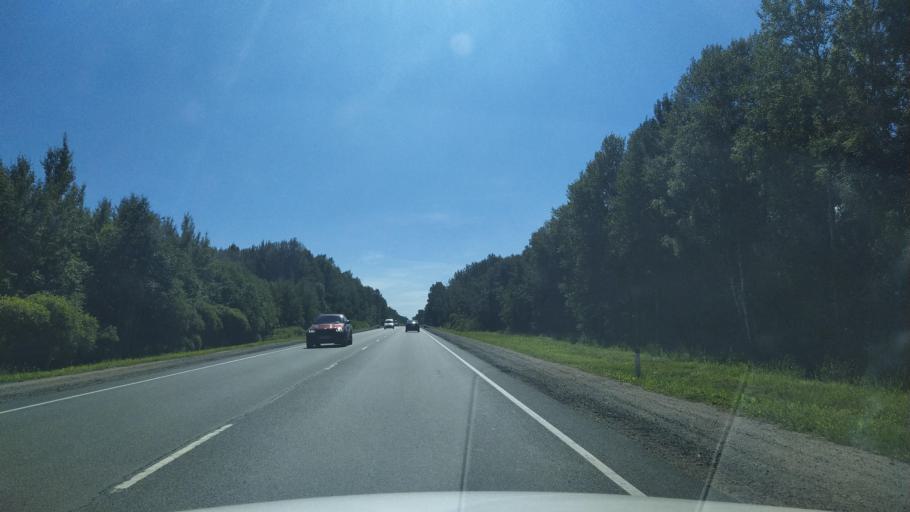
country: RU
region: Pskov
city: Pskov
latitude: 57.7767
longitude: 28.4003
